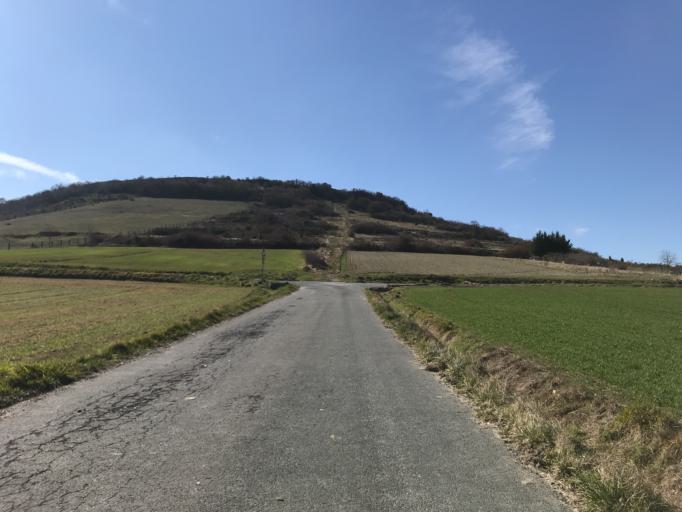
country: ES
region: Basque Country
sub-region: Provincia de Alava
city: Gasteiz / Vitoria
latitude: 42.8176
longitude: -2.6556
